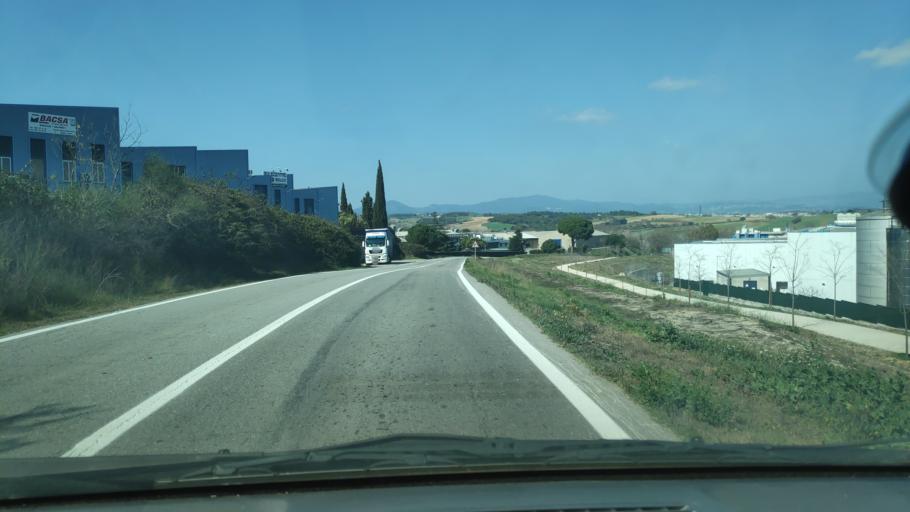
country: ES
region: Catalonia
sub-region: Provincia de Barcelona
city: Polinya
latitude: 41.5281
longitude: 2.1528
